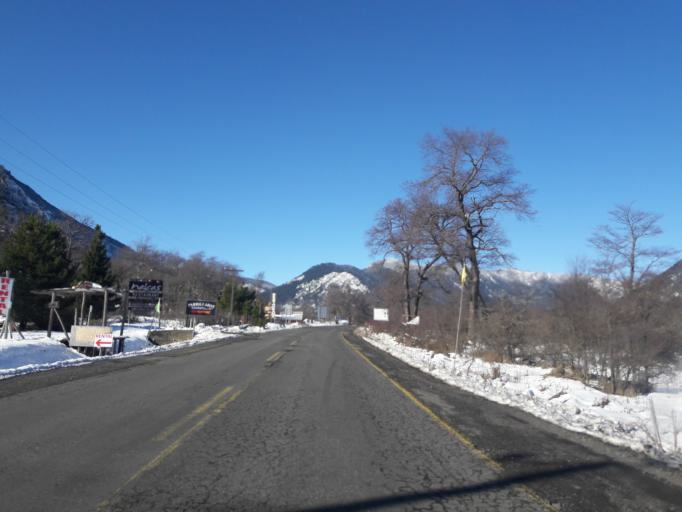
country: CL
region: Araucania
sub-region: Provincia de Cautin
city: Vilcun
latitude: -38.4723
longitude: -71.5633
